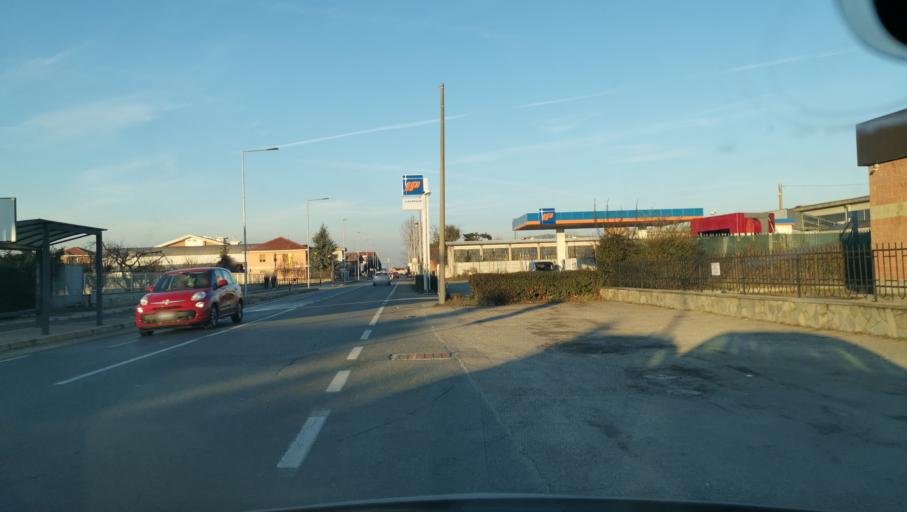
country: IT
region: Piedmont
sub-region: Provincia di Torino
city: Gerbole-Zucche
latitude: 44.9811
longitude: 7.5266
